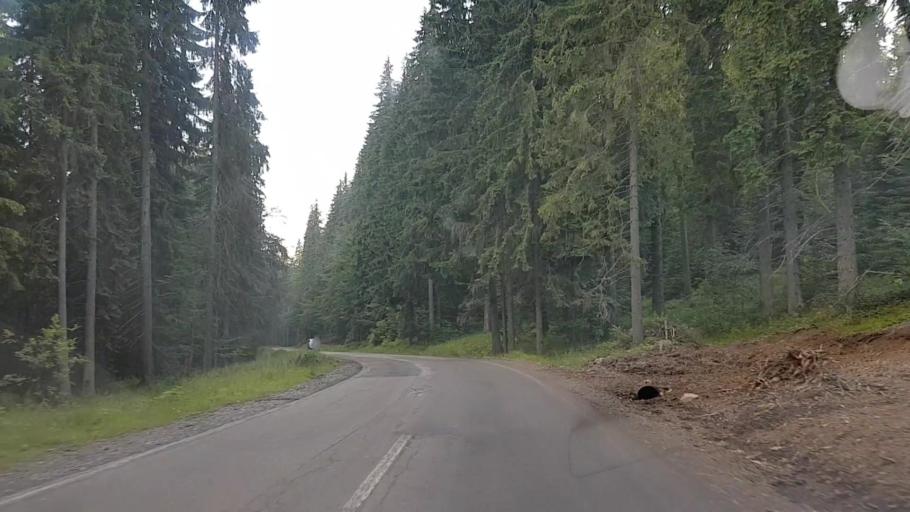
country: RO
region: Harghita
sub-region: Comuna Varsag
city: Varsag
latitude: 46.6521
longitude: 25.2907
